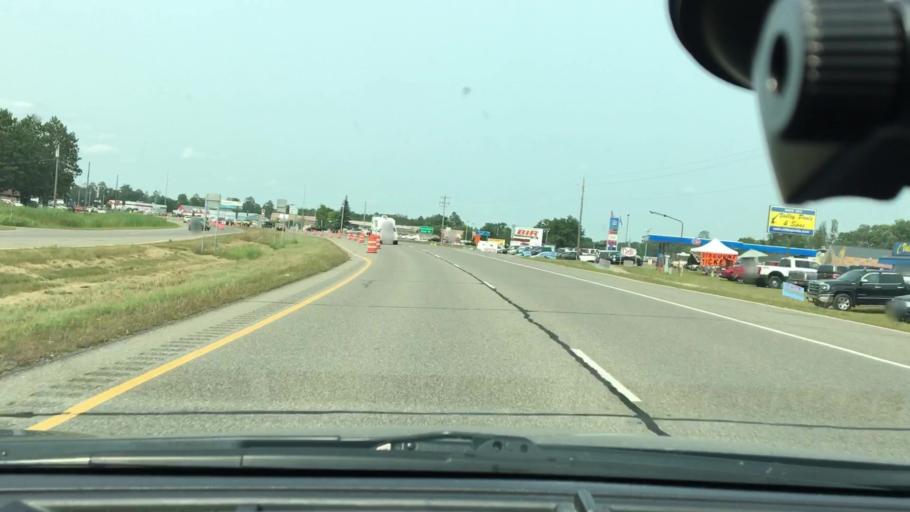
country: US
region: Minnesota
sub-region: Cass County
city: East Gull Lake
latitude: 46.4153
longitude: -94.2857
